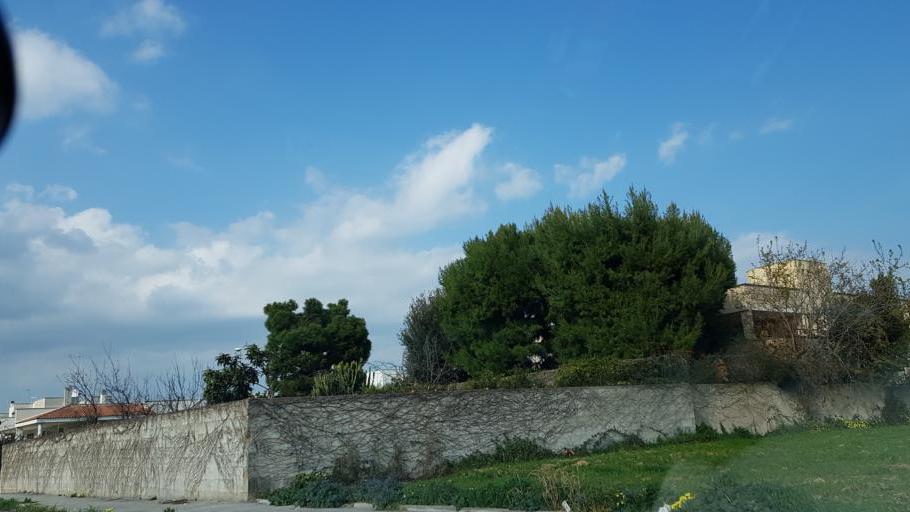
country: IT
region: Apulia
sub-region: Provincia di Brindisi
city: Brindisi
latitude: 40.6457
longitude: 17.9303
